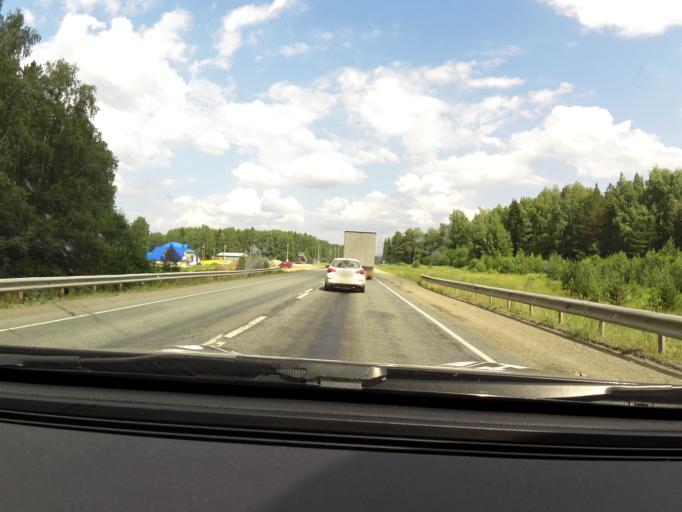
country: RU
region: Sverdlovsk
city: Bisert'
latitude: 56.8284
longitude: 59.0120
